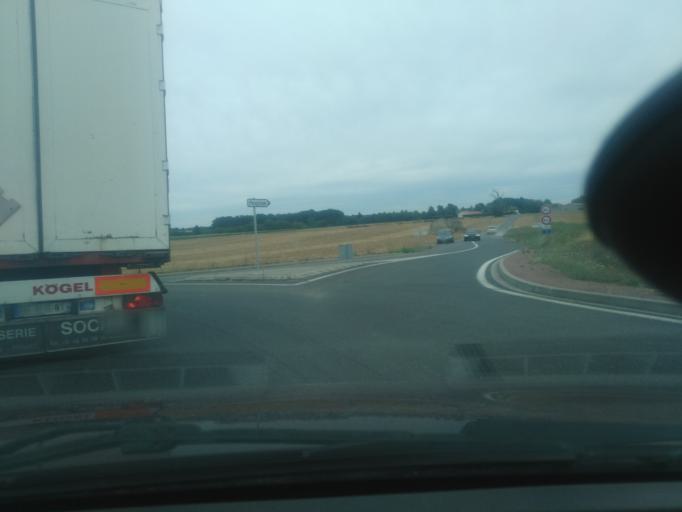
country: FR
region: Poitou-Charentes
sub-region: Departement de la Vienne
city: Sevres-Anxaumont
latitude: 46.5587
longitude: 0.4851
